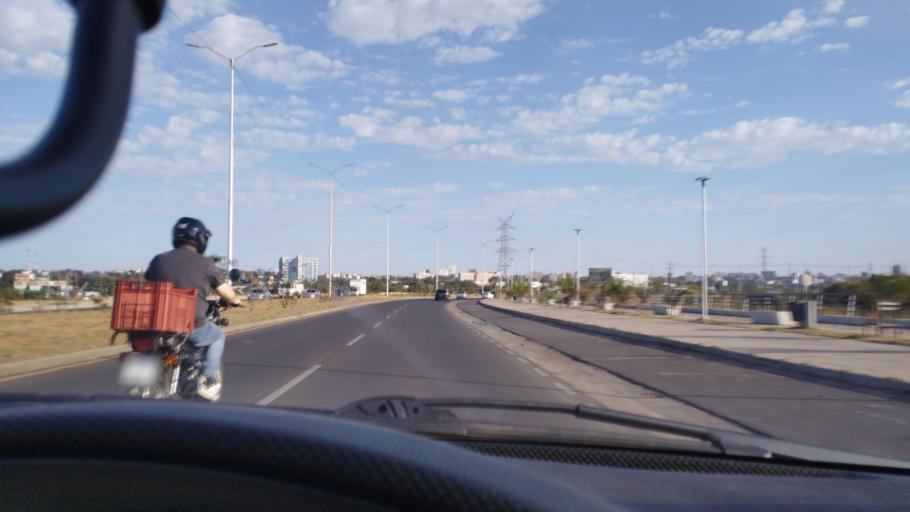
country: PY
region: Asuncion
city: Asuncion
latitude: -25.2601
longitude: -57.6079
